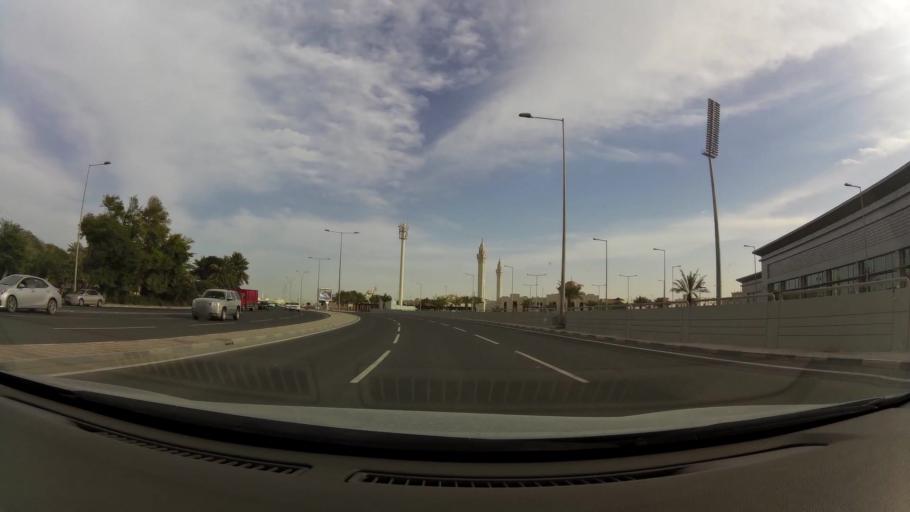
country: QA
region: Baladiyat ad Dawhah
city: Doha
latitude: 25.2523
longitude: 51.5363
